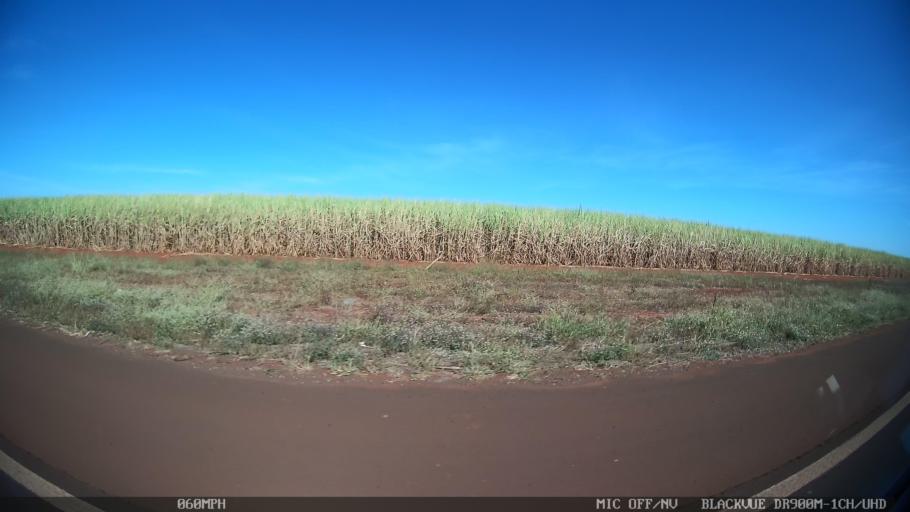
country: BR
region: Sao Paulo
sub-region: Guaira
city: Guaira
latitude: -20.4444
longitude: -48.2749
